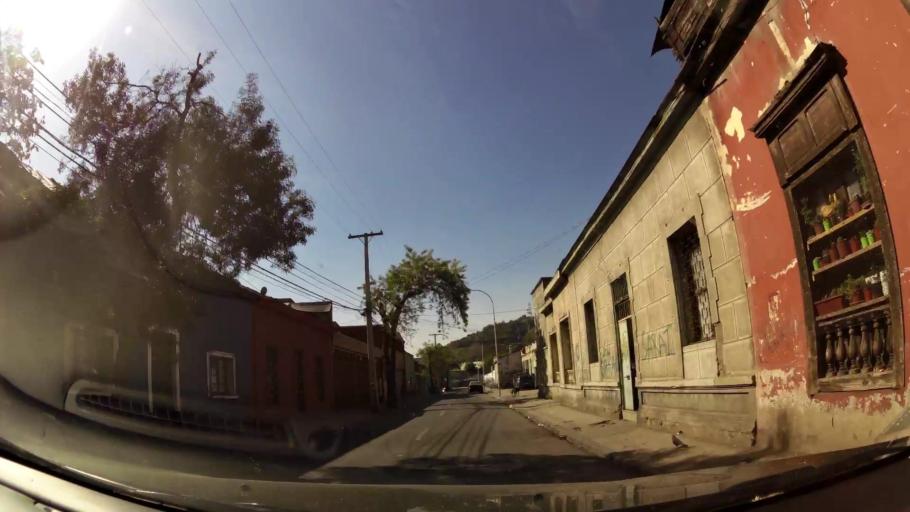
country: CL
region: Santiago Metropolitan
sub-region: Provincia de Santiago
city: Santiago
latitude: -33.4251
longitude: -70.6493
